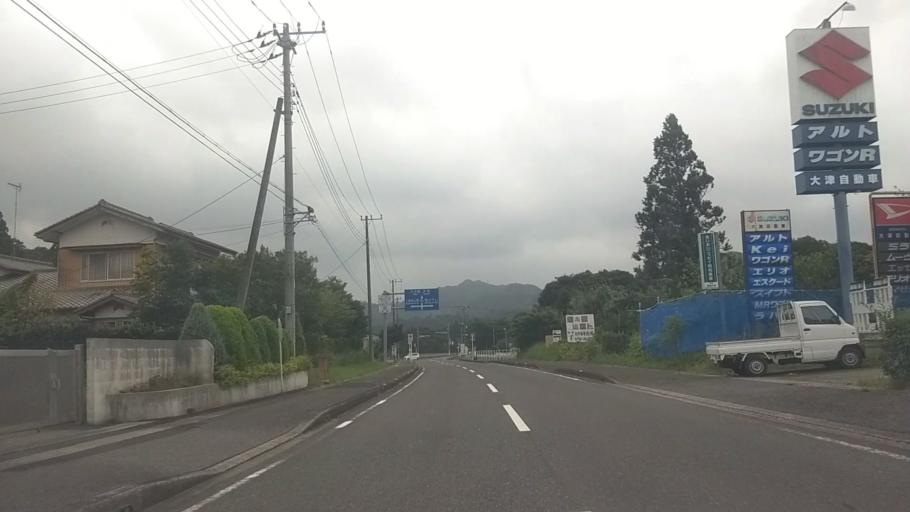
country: JP
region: Chiba
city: Kawaguchi
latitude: 35.2321
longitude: 140.0873
